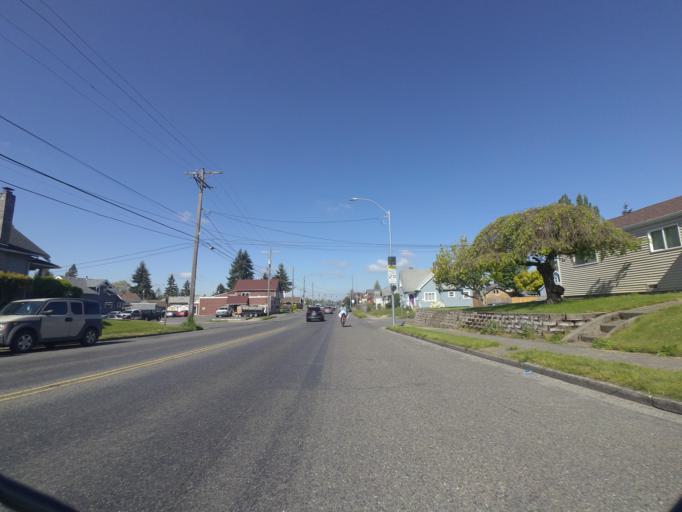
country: US
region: Washington
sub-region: Pierce County
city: Tacoma
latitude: 47.2065
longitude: -122.4453
